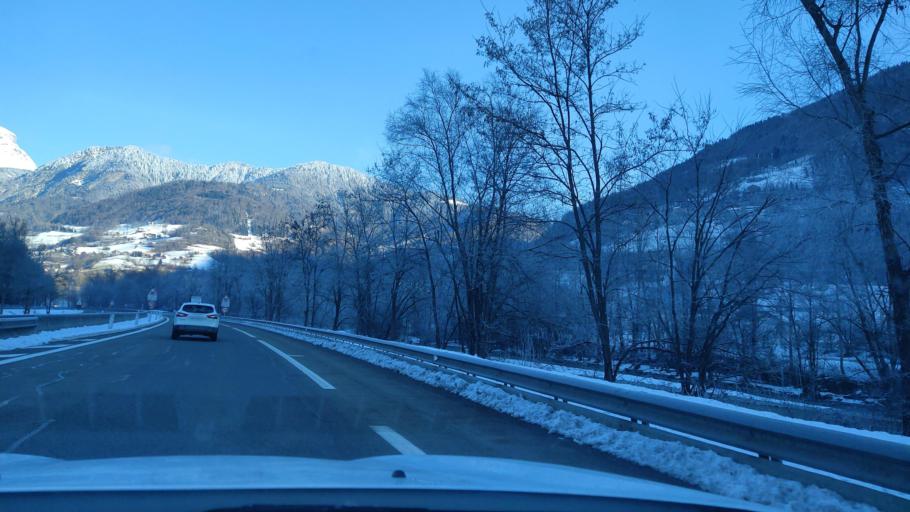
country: FR
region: Rhone-Alpes
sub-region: Departement de la Savoie
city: Marthod
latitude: 45.7353
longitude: 6.4228
